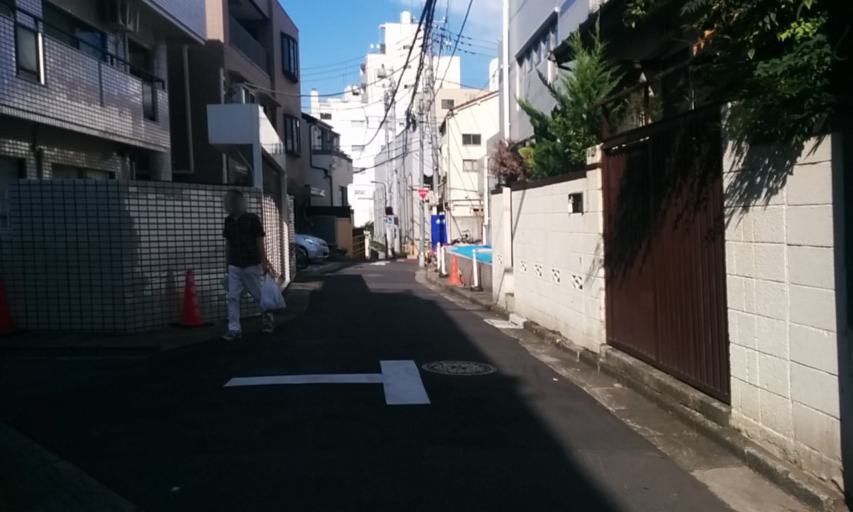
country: JP
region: Tokyo
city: Tokyo
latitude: 35.7127
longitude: 139.6995
